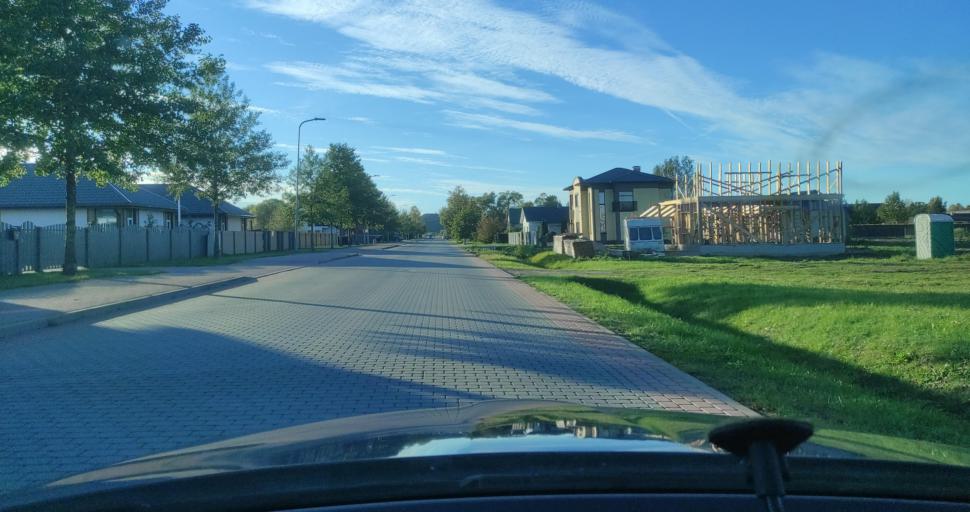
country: LV
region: Ventspils
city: Ventspils
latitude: 57.3659
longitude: 21.5716
